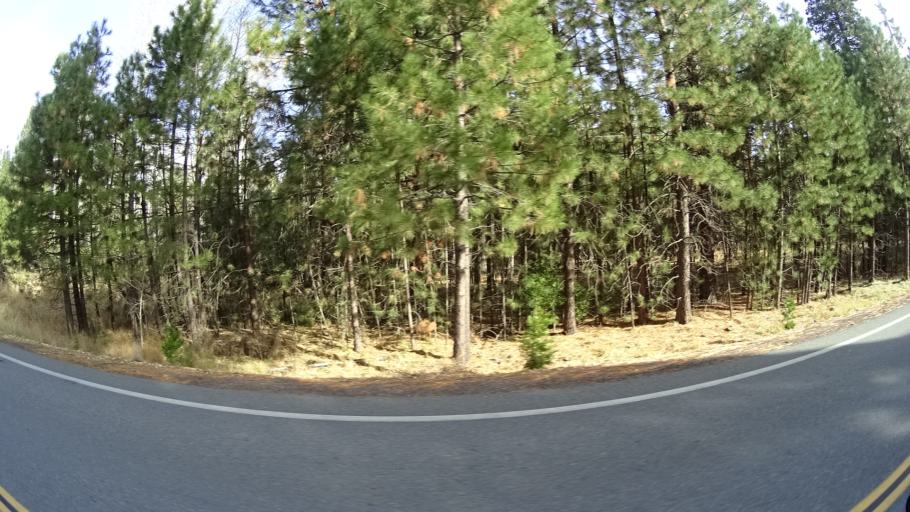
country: US
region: California
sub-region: Siskiyou County
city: Weed
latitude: 41.3885
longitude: -122.4097
